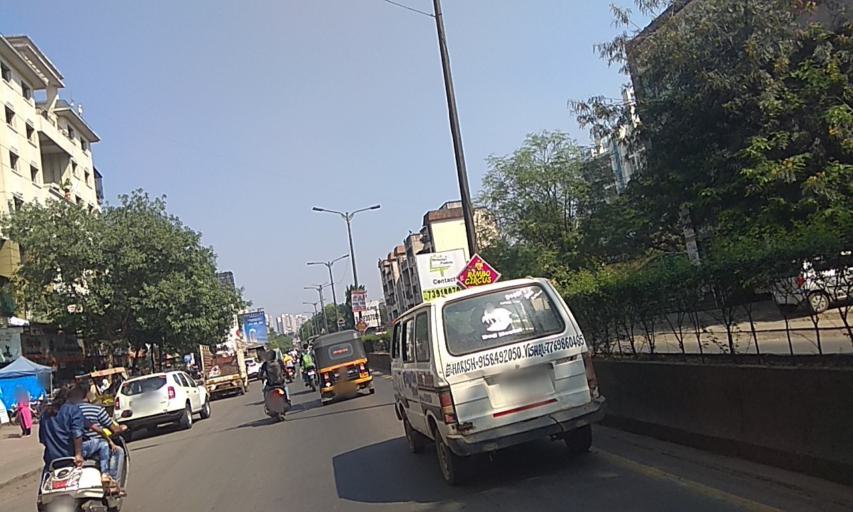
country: IN
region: Maharashtra
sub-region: Pune Division
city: Pune
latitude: 18.5066
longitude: 73.9281
